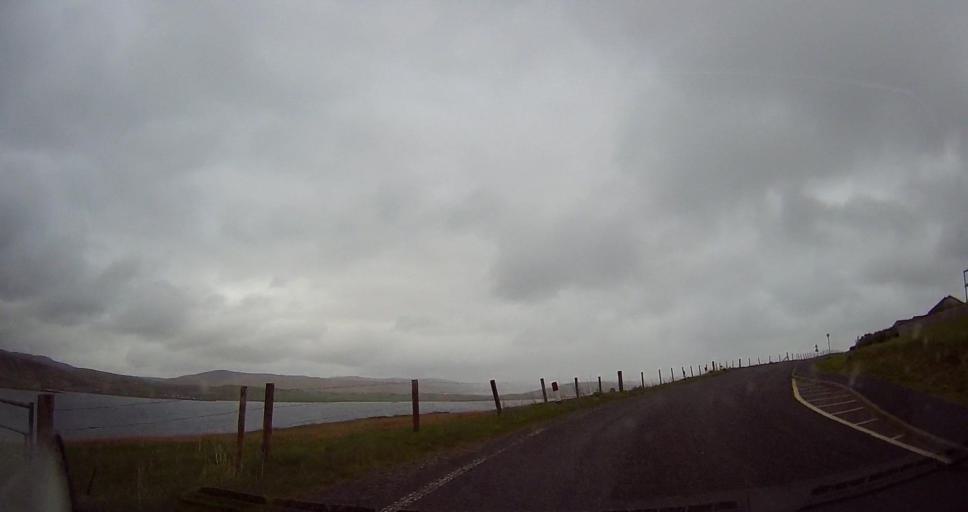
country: GB
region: Scotland
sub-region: Shetland Islands
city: Lerwick
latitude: 60.3907
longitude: -1.3695
